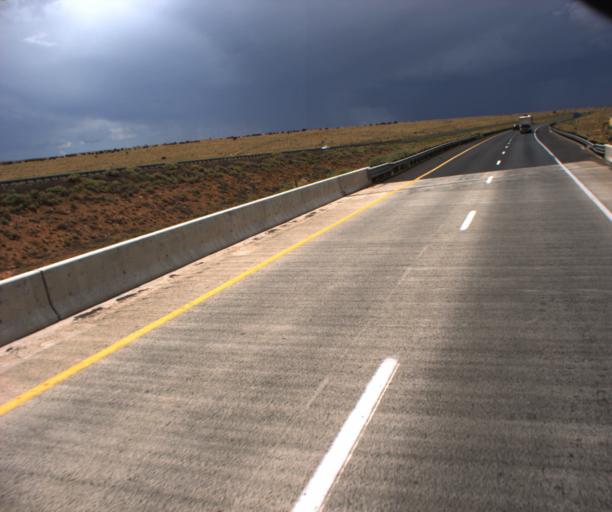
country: US
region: Arizona
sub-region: Coconino County
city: LeChee
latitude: 35.1003
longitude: -110.9748
